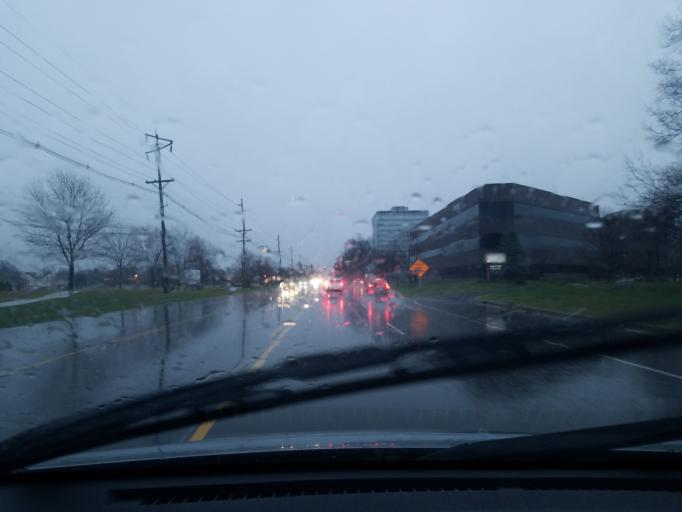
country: US
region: Kentucky
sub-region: Jefferson County
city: Hurstbourne
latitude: 38.2470
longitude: -85.5833
